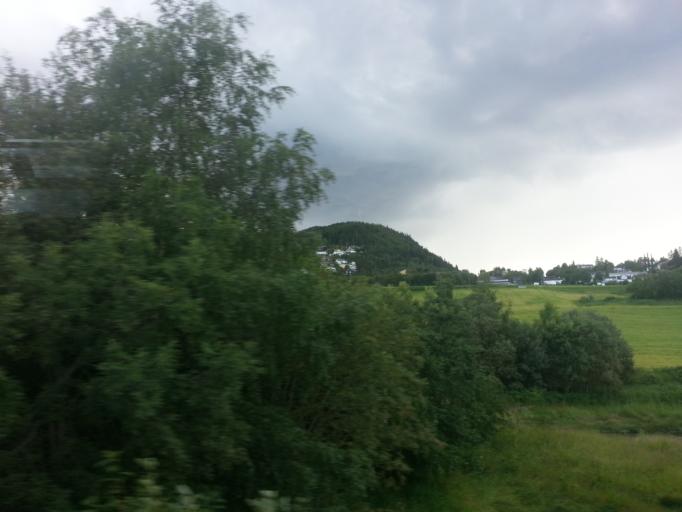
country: NO
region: Sor-Trondelag
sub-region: Malvik
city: Malvik
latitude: 63.4378
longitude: 10.6113
